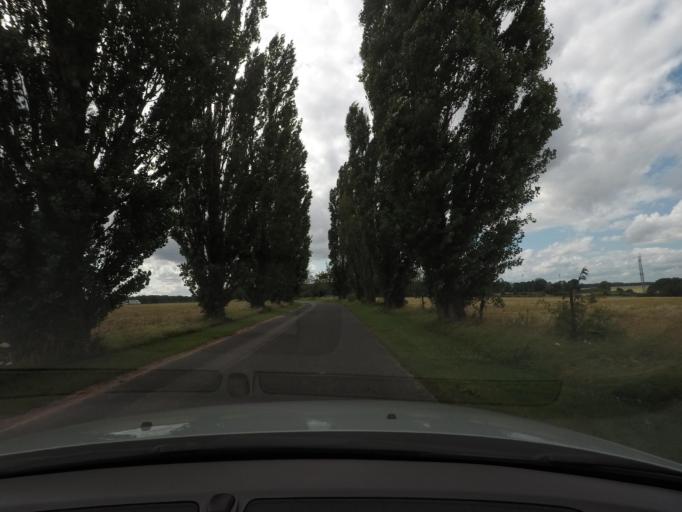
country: FR
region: Haute-Normandie
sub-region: Departement de l'Eure
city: Les Andelys
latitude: 49.2375
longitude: 1.4208
